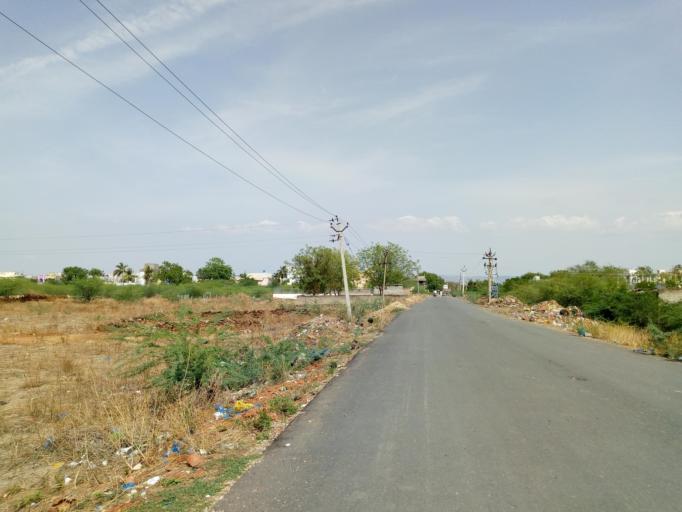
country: IN
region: Andhra Pradesh
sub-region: Prakasam
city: Cumbum
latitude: 15.5853
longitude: 79.1082
